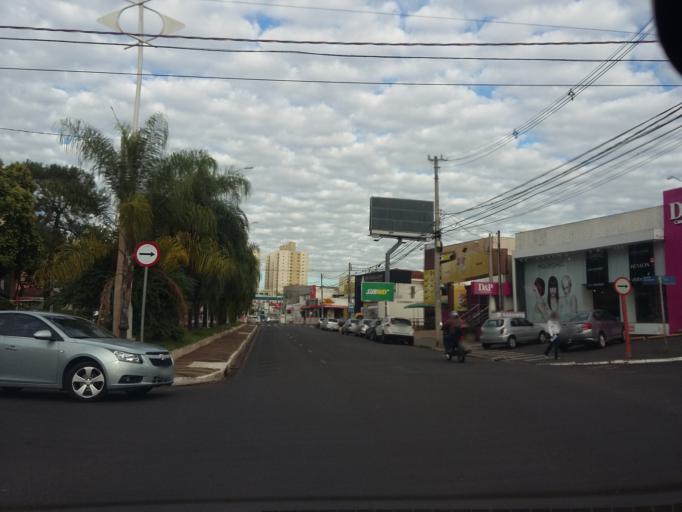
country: BR
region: Sao Paulo
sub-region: Sao Jose Do Rio Preto
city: Sao Jose do Rio Preto
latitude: -20.8127
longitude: -49.3888
